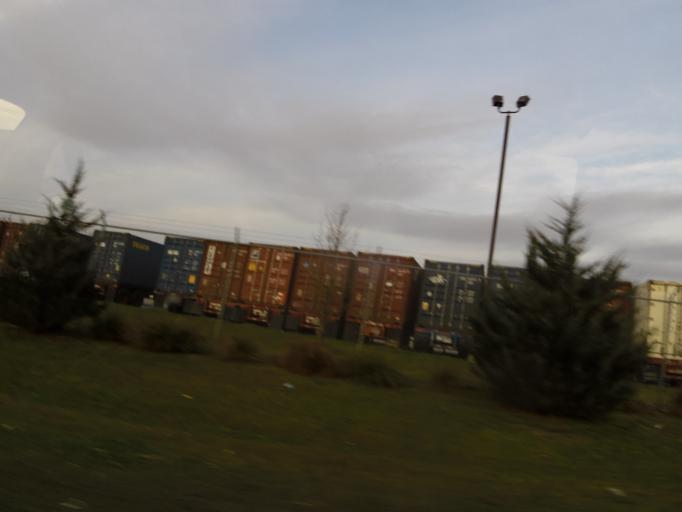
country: US
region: Florida
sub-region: Duval County
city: Jacksonville
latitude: 30.3664
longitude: -81.7164
